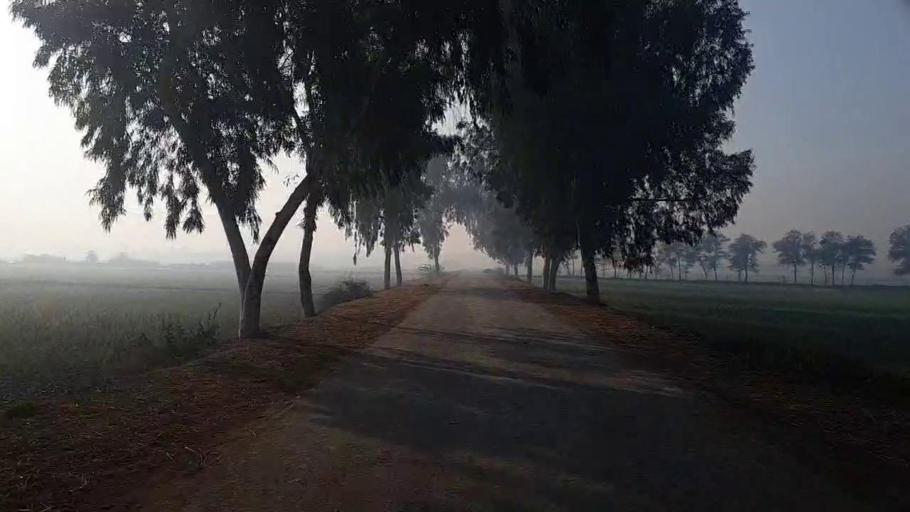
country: PK
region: Sindh
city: Mehar
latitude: 27.1407
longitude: 67.8231
